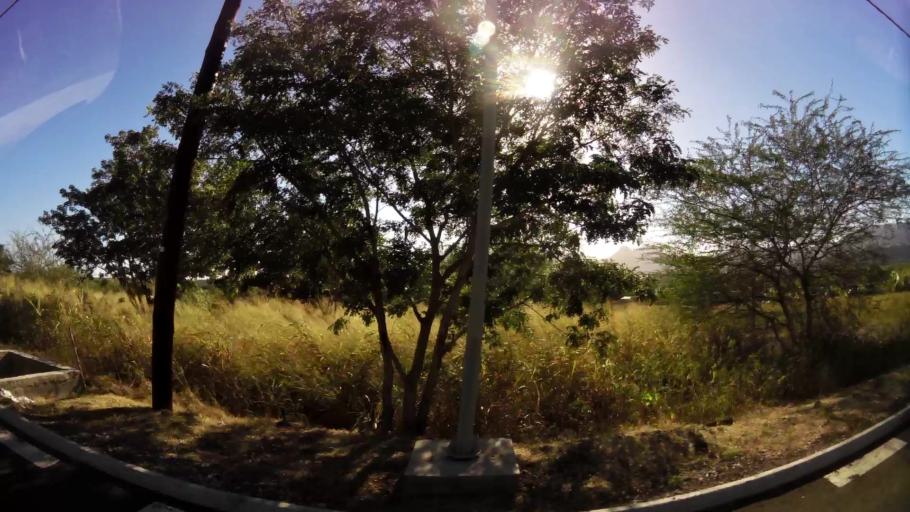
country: MU
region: Black River
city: Tamarin
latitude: -20.3404
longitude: 57.3873
